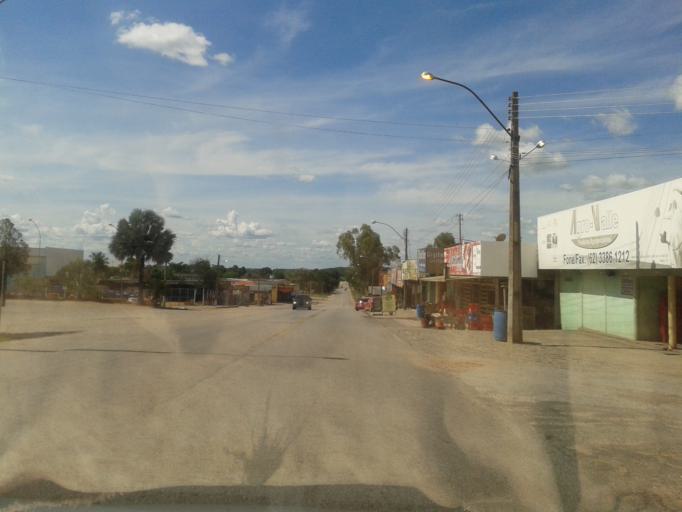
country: BR
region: Goias
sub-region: Itapuranga
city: Itapuranga
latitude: -15.4475
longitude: -50.3636
